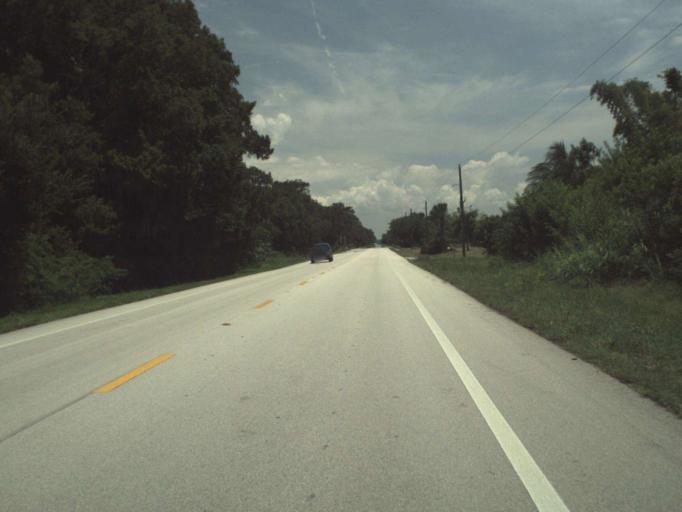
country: US
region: Florida
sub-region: Martin County
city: Indiantown
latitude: 27.0387
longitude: -80.6379
